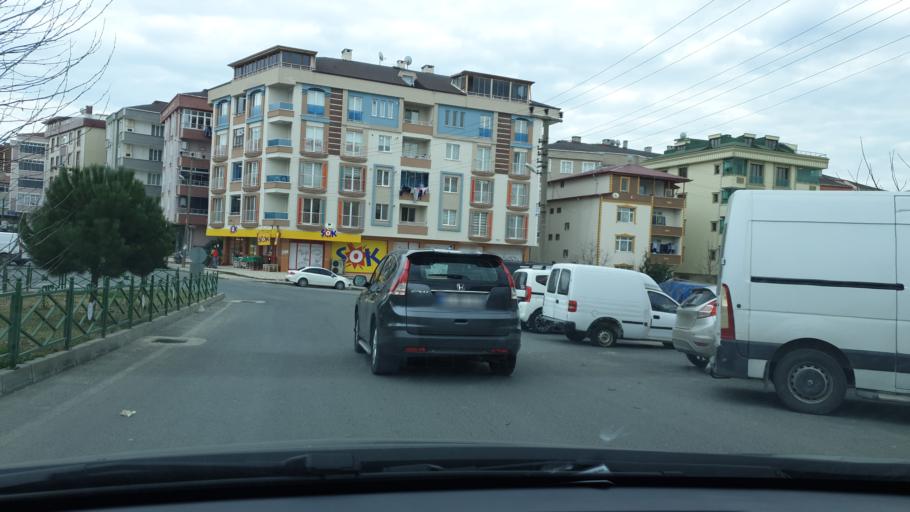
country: TR
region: Tekirdag
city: Cerkezkoey
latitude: 41.2841
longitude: 27.9884
